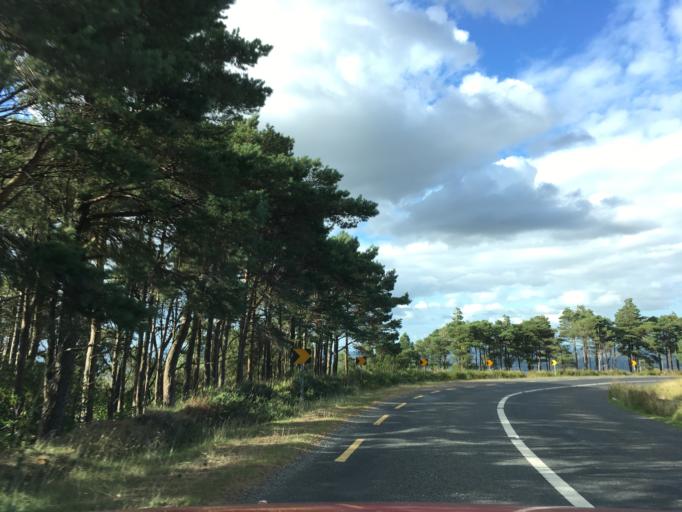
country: IE
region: Munster
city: Cahir
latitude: 52.2559
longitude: -7.9555
